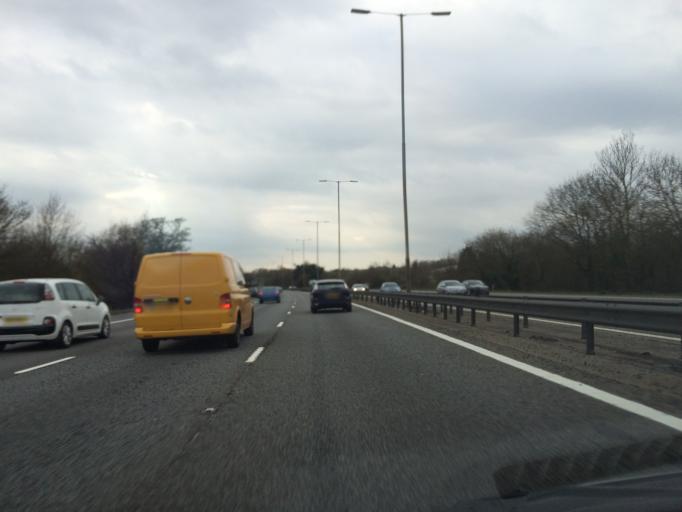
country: GB
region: England
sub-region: Wokingham
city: Lower Earley
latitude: 51.4205
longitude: -0.9234
